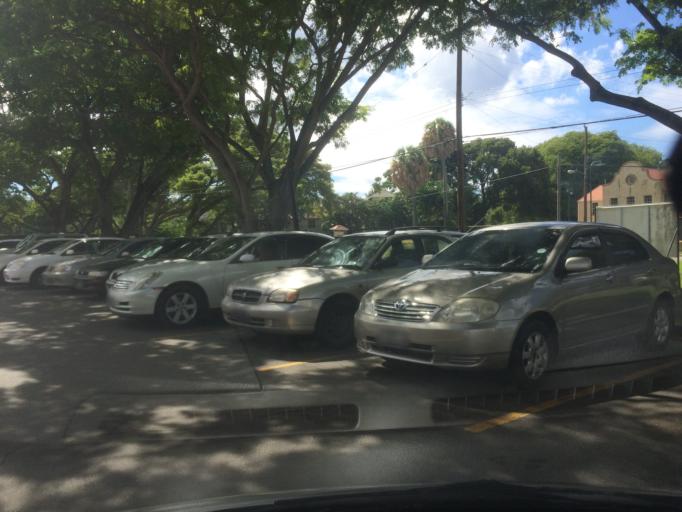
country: BB
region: Saint James
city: Holetown
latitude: 13.1786
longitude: -59.6377
